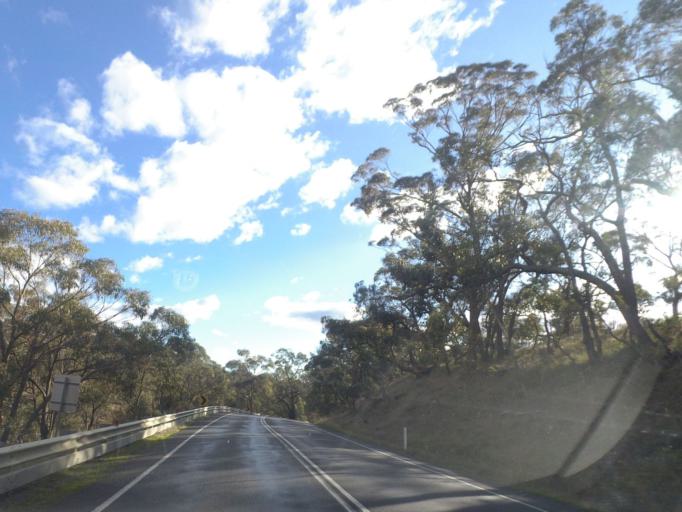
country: AU
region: Victoria
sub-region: Mount Alexander
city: Castlemaine
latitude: -37.1052
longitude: 144.3040
